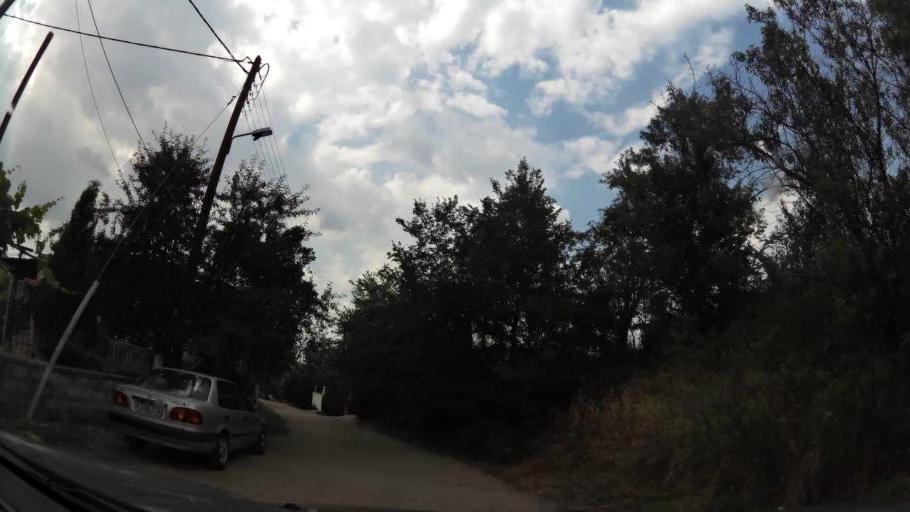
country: GR
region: West Macedonia
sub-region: Nomos Kozanis
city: Koila
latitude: 40.3480
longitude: 21.8301
